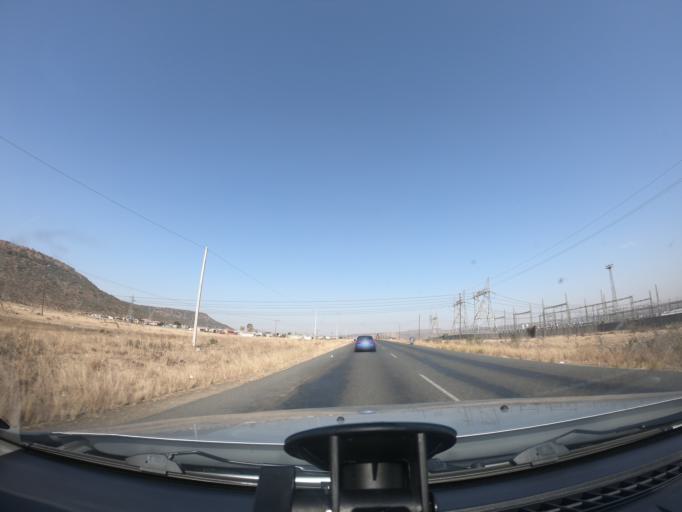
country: ZA
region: KwaZulu-Natal
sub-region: uThukela District Municipality
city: Ladysmith
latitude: -28.5662
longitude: 29.8356
